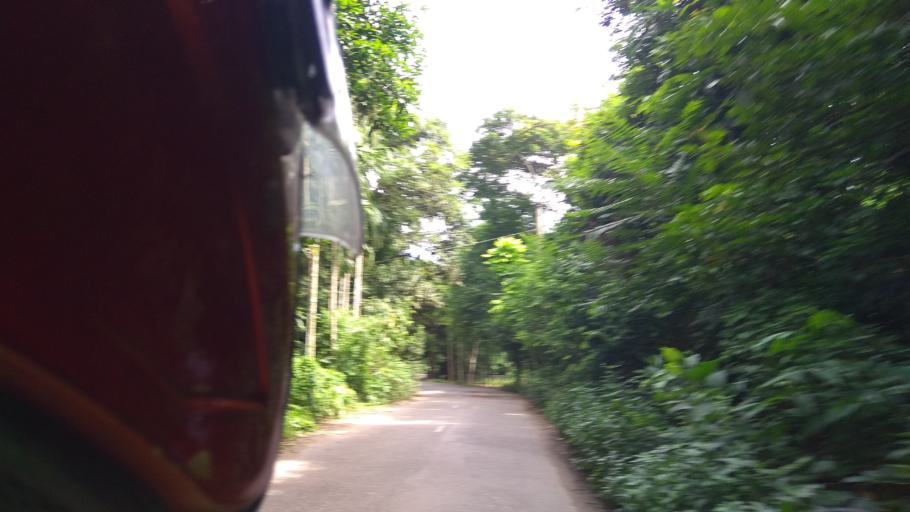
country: BD
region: Khulna
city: Kalia
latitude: 23.1329
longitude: 89.6413
